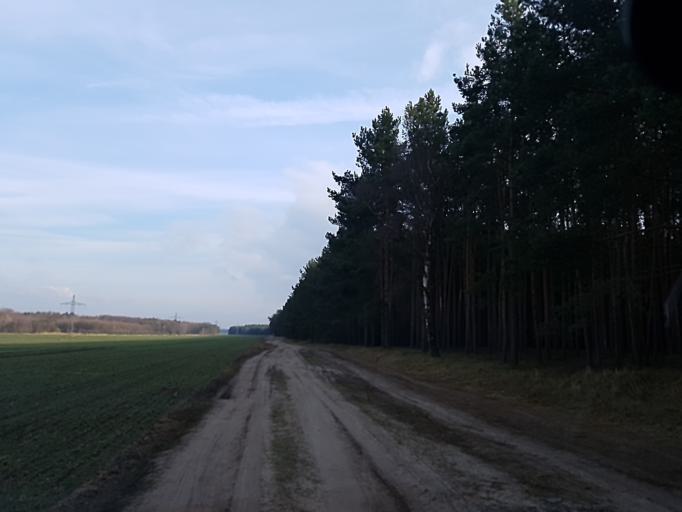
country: DE
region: Brandenburg
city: Wollin
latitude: 52.2670
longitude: 12.5017
